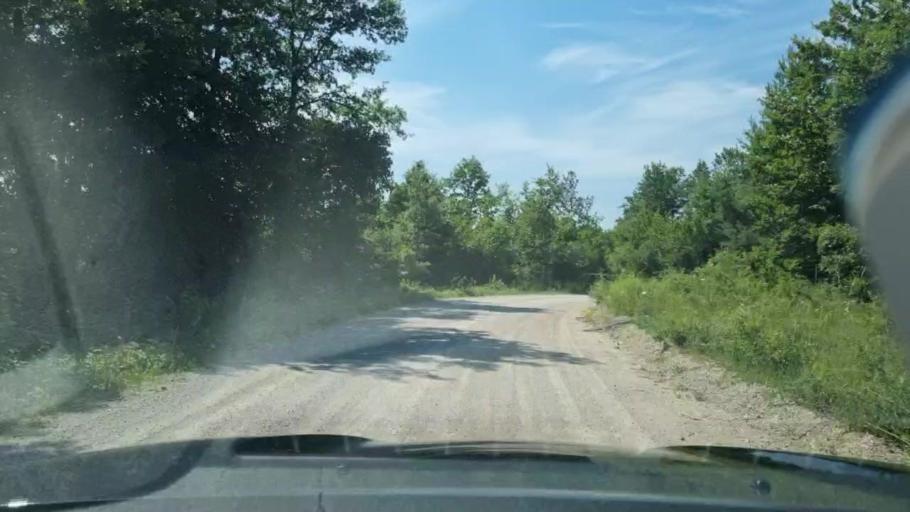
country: BA
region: Federation of Bosnia and Herzegovina
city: Orasac
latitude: 44.6183
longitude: 16.3034
